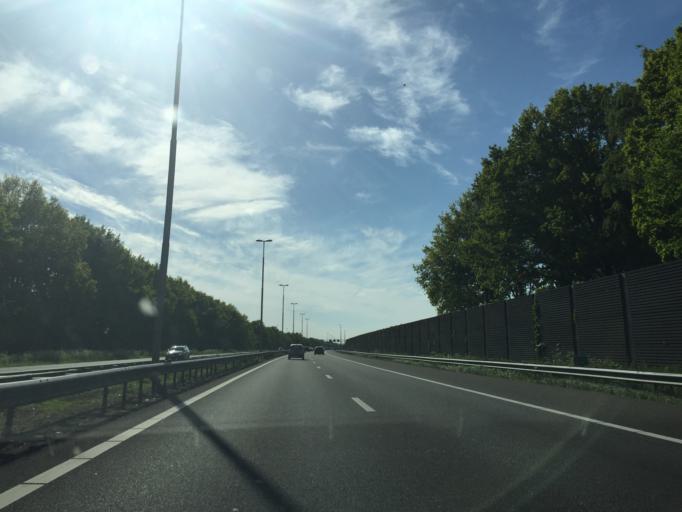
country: NL
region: Gelderland
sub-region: Gemeente Barneveld
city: Terschuur
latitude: 52.1628
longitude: 5.5159
